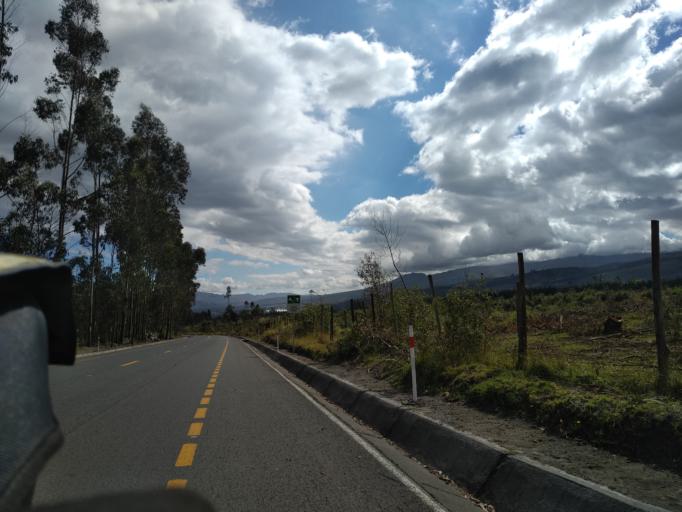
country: EC
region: Cotopaxi
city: Saquisili
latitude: -0.6987
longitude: -78.5743
